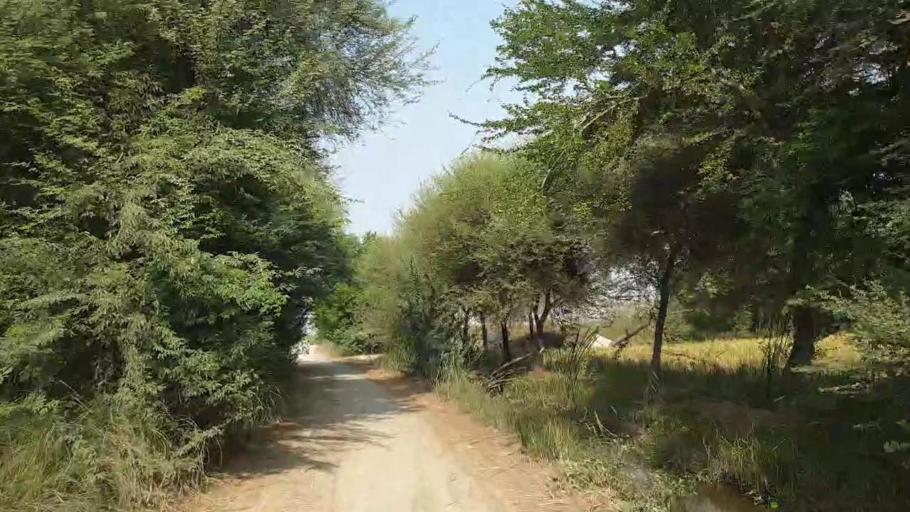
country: PK
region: Sindh
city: Matli
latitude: 24.9512
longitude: 68.5565
